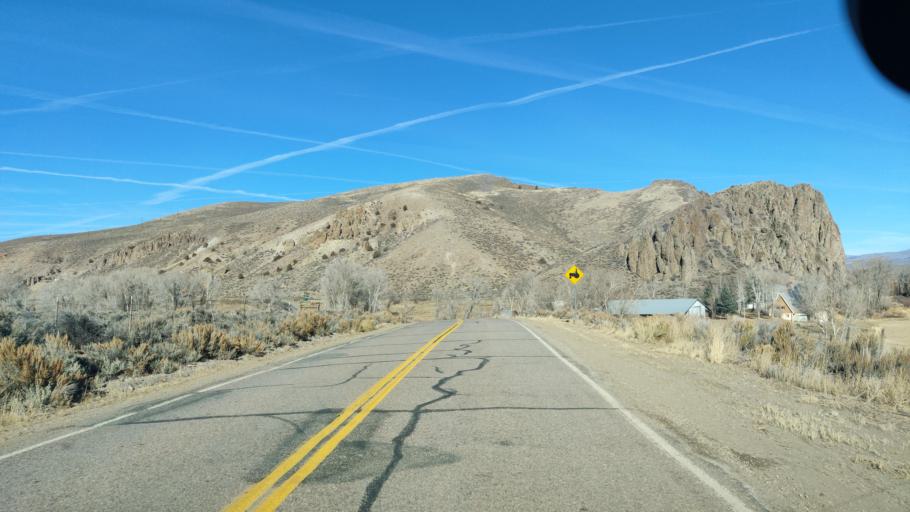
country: US
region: Colorado
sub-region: Gunnison County
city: Gunnison
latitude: 38.5527
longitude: -106.9499
